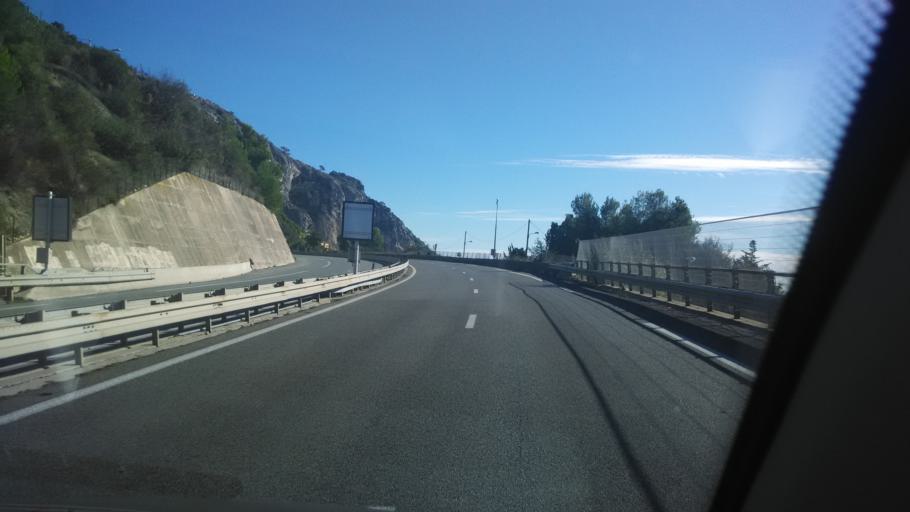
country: FR
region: Provence-Alpes-Cote d'Azur
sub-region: Departement des Alpes-Maritimes
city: Menton
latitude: 43.7905
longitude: 7.5153
